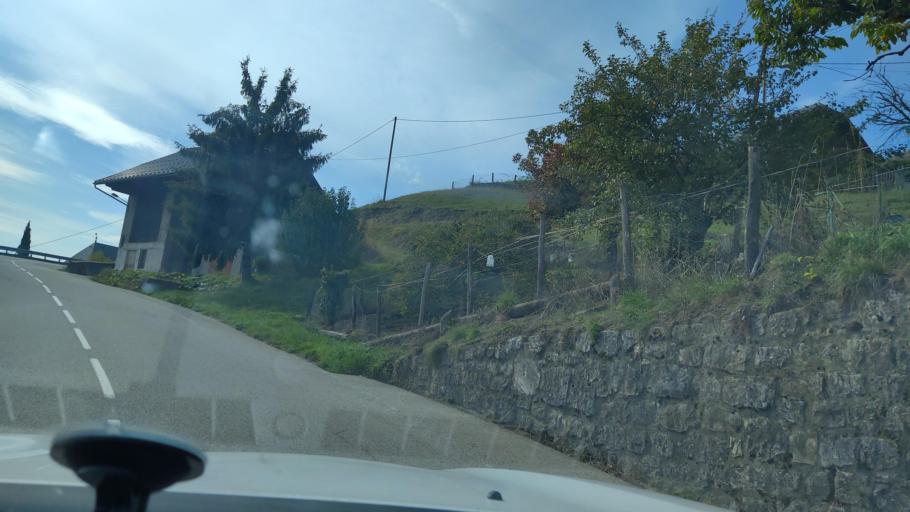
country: FR
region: Rhone-Alpes
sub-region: Departement de la Savoie
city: Coise-Saint-Jean-Pied-Gauthier
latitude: 45.5784
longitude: 6.1534
